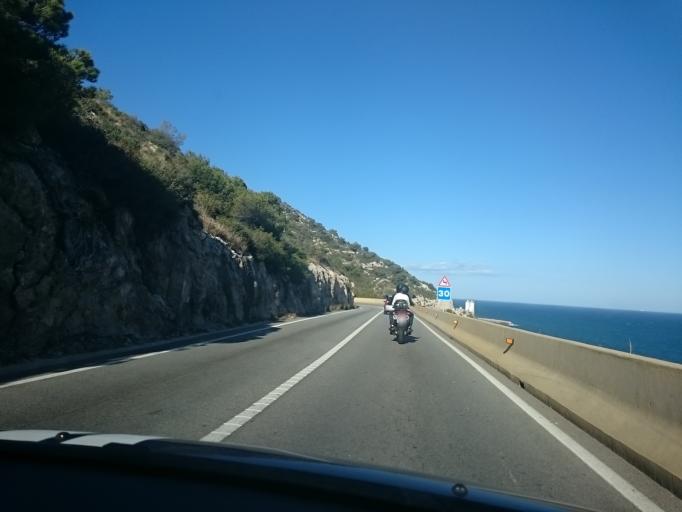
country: ES
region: Catalonia
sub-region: Provincia de Barcelona
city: Sitges
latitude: 41.2352
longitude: 1.8539
